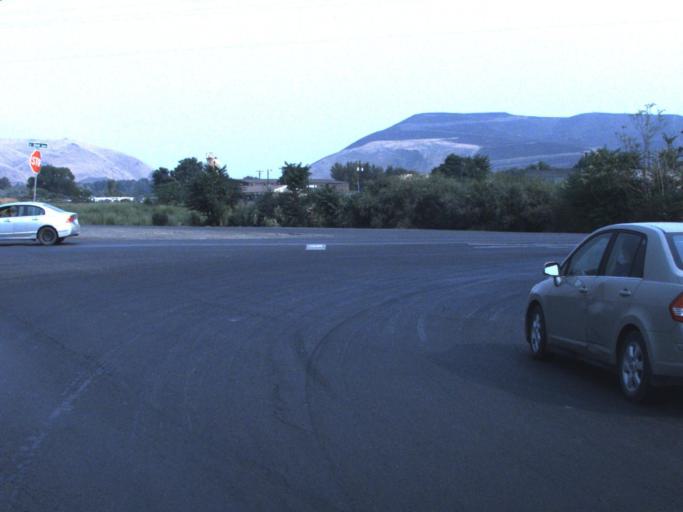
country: US
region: Washington
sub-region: Yakima County
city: Union Gap
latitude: 46.5036
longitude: -120.4671
